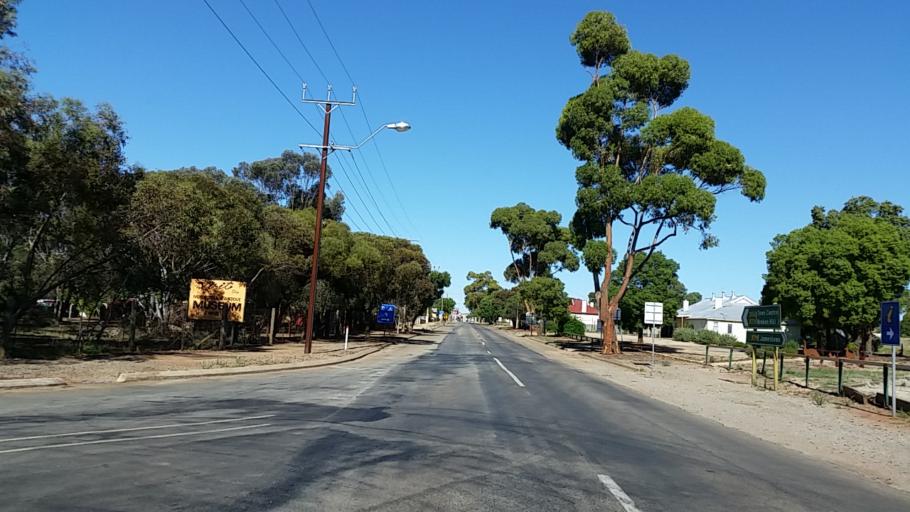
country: AU
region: South Australia
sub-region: Peterborough
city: Peterborough
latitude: -32.9741
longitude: 138.8288
